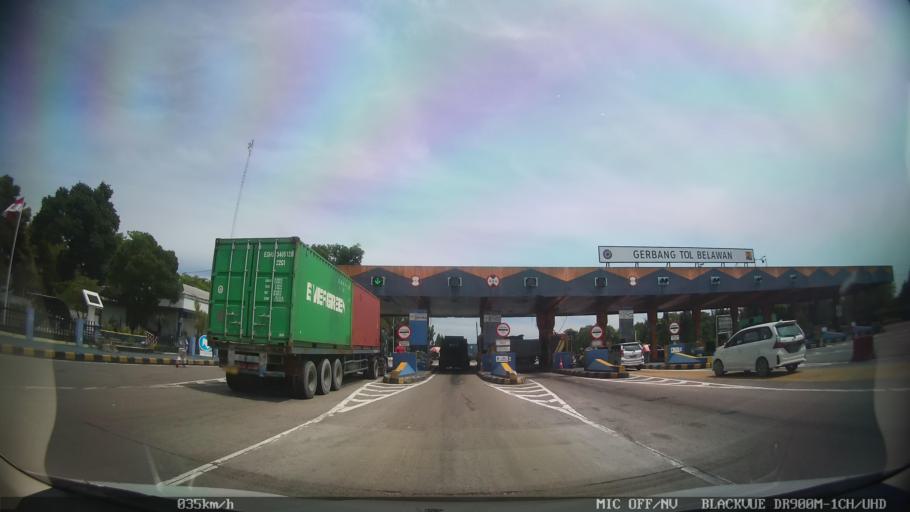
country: ID
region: North Sumatra
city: Labuhan Deli
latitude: 3.7292
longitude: 98.6809
